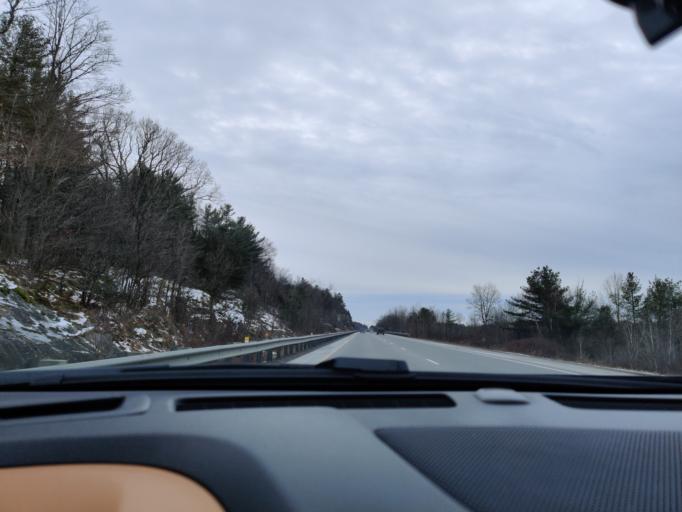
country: US
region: New York
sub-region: Jefferson County
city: Alexandria Bay
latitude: 44.4107
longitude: -75.9273
